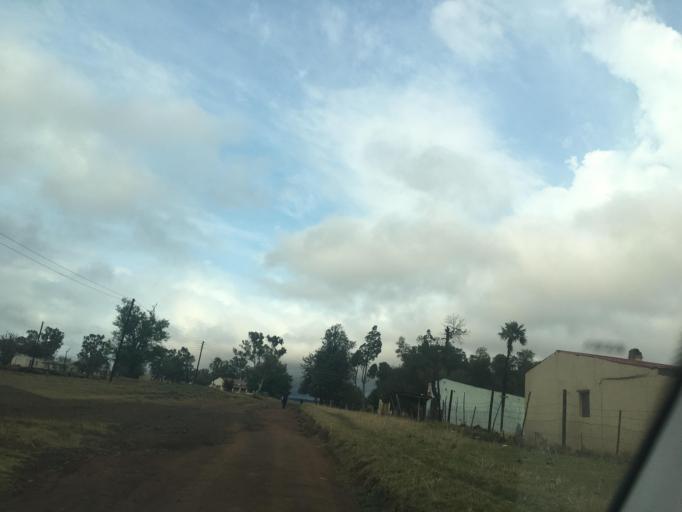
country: ZA
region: Eastern Cape
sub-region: Chris Hani District Municipality
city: Cala
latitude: -31.5238
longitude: 27.7016
